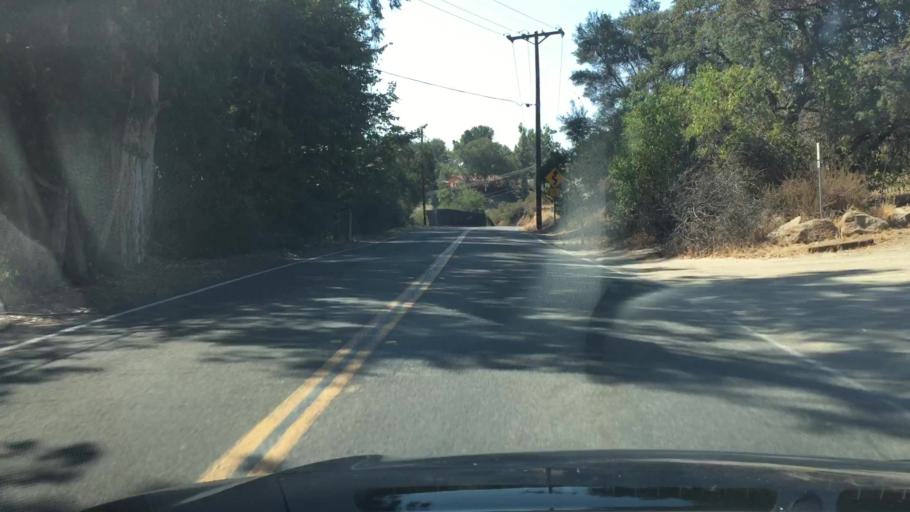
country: US
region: California
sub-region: San Diego County
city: Jamul
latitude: 32.7294
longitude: -116.8727
